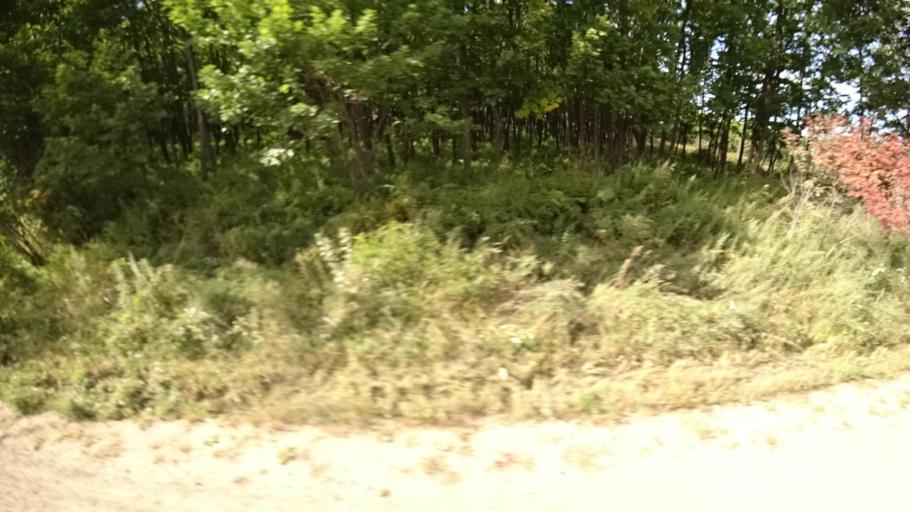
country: RU
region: Primorskiy
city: Yakovlevka
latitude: 44.3852
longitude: 133.5379
